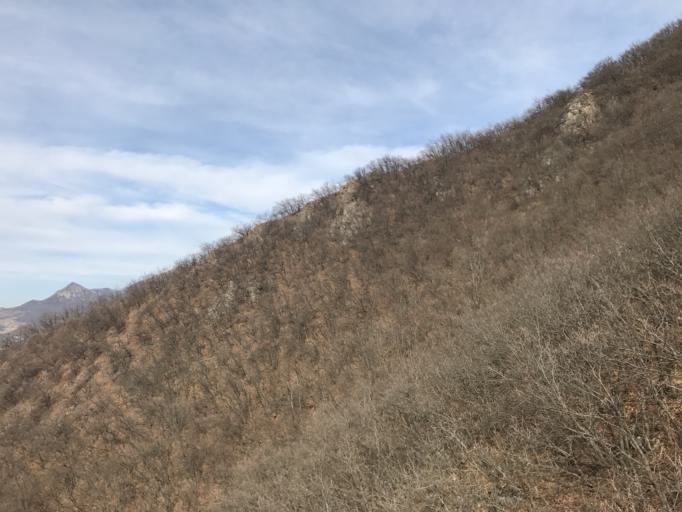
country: RU
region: Stavropol'skiy
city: Goryachevodskiy
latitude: 44.0475
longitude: 43.0860
